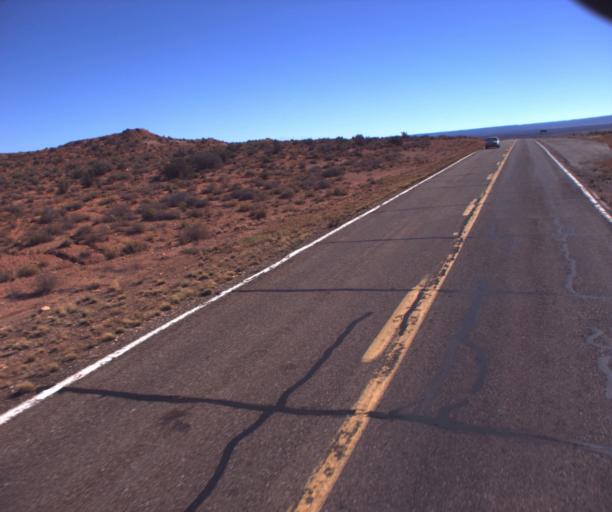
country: US
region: Arizona
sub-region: Coconino County
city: Fredonia
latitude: 36.9310
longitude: -112.4943
